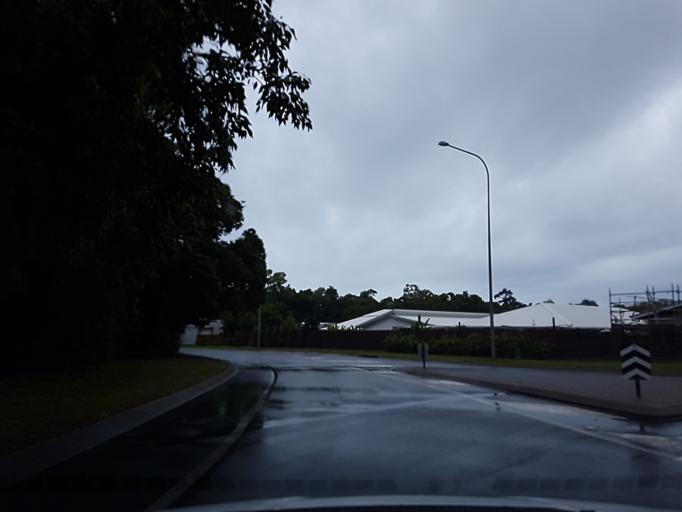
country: AU
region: Queensland
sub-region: Cairns
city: Palm Cove
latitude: -16.7550
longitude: 145.6647
